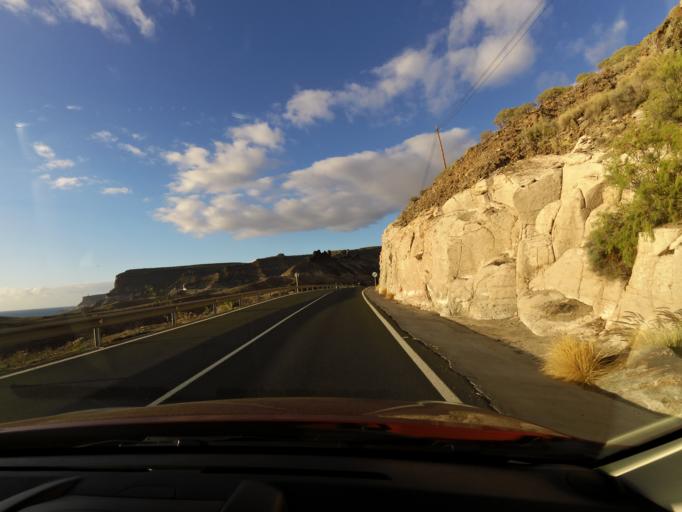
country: ES
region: Canary Islands
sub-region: Provincia de Las Palmas
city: Puerto Rico
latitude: 27.7995
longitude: -15.7366
